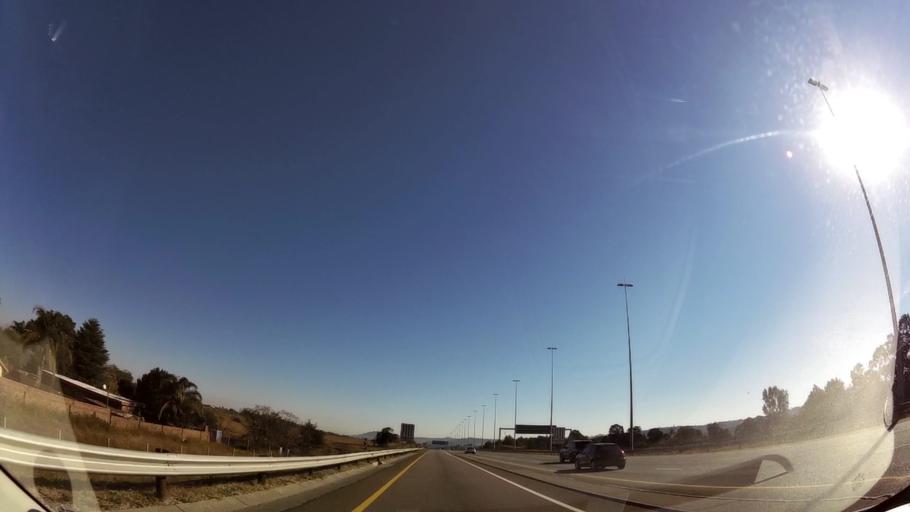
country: ZA
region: Gauteng
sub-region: City of Tshwane Metropolitan Municipality
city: Centurion
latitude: -25.8248
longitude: 28.2409
